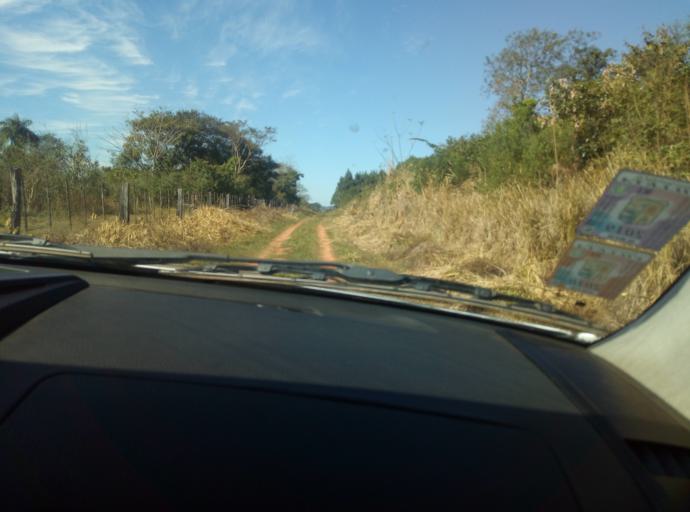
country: PY
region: Caaguazu
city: Carayao
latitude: -25.1759
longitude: -56.3052
